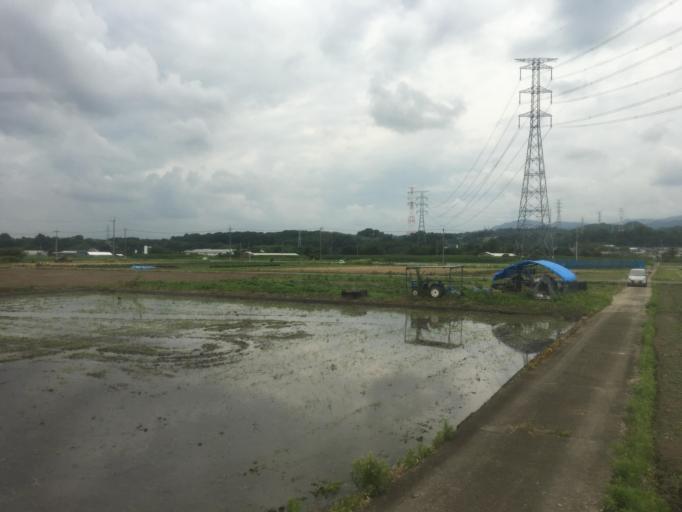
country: JP
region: Gunma
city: Yoshii
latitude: 36.2639
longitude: 139.0164
